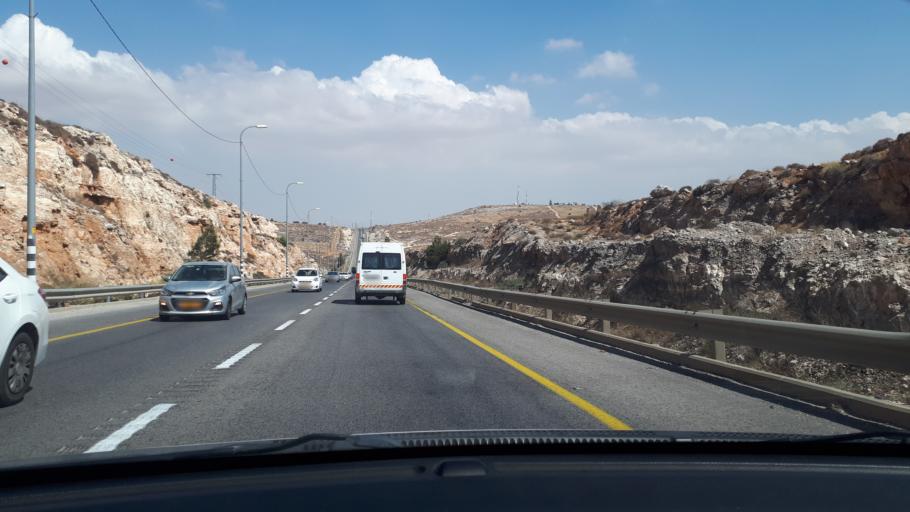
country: PS
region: West Bank
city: Burqah
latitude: 31.8996
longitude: 35.2635
